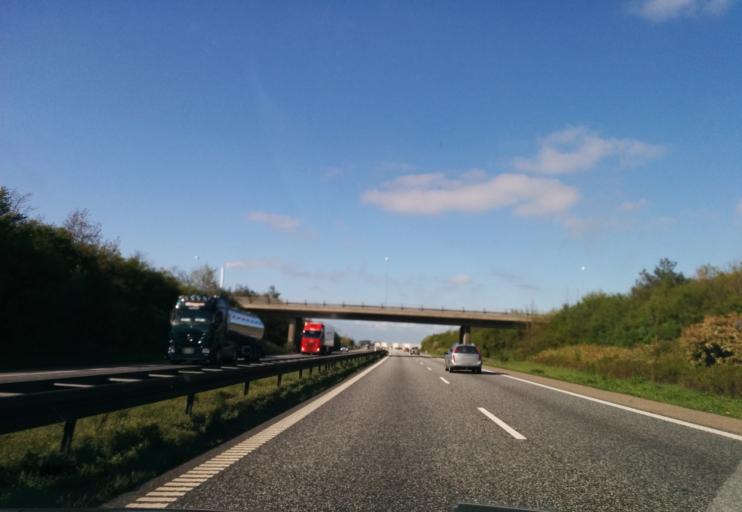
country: DK
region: Central Jutland
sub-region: Hedensted Kommune
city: Hedensted
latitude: 55.7901
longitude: 9.6685
